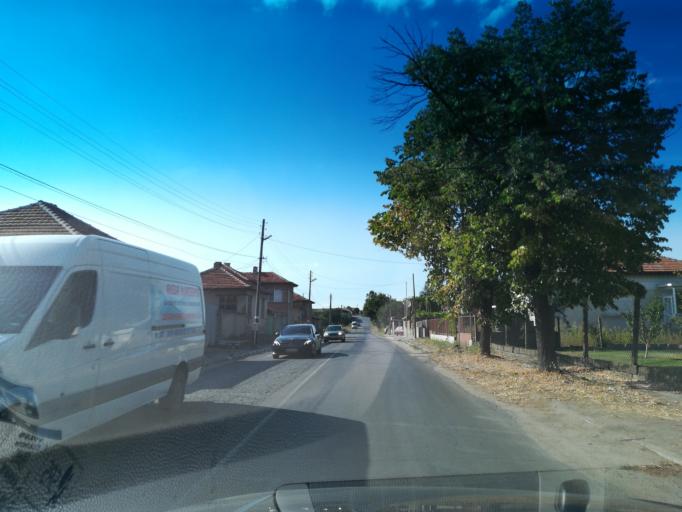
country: BG
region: Khaskovo
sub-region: Obshtina Mineralni Bani
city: Mineralni Bani
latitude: 42.0190
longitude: 25.4164
